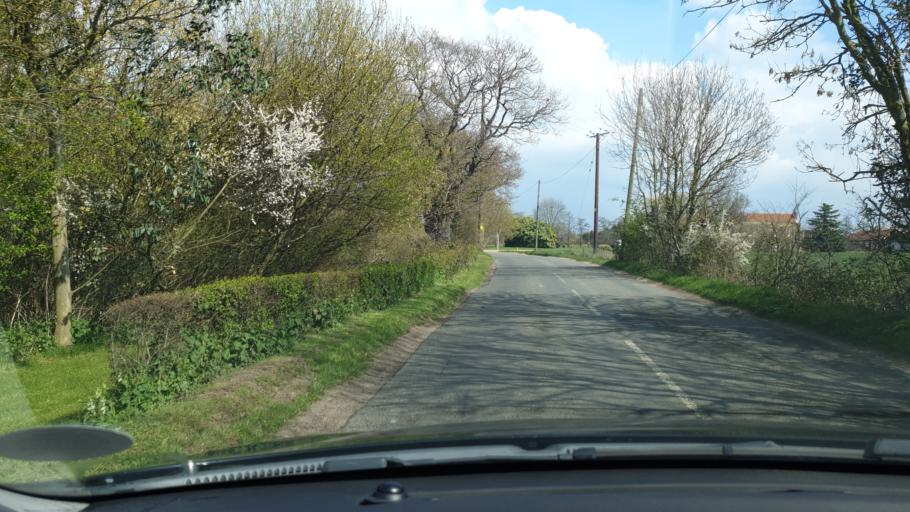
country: GB
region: England
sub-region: Essex
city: Great Bentley
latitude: 51.8659
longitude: 1.1007
